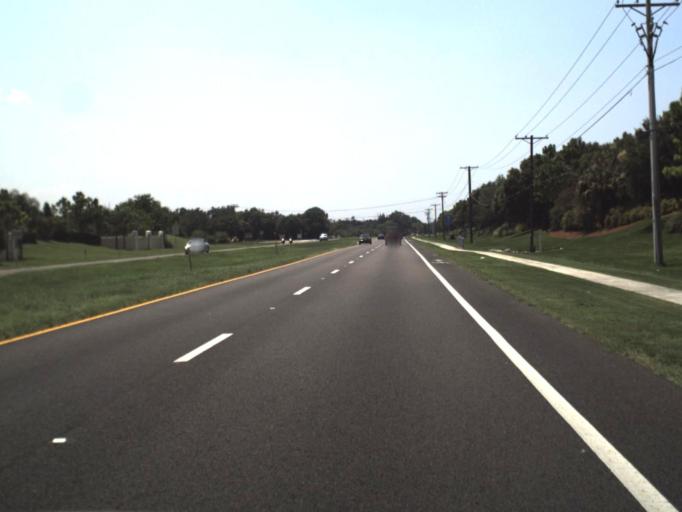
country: US
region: Florida
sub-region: Hillsborough County
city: Apollo Beach
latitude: 27.7462
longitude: -82.4167
